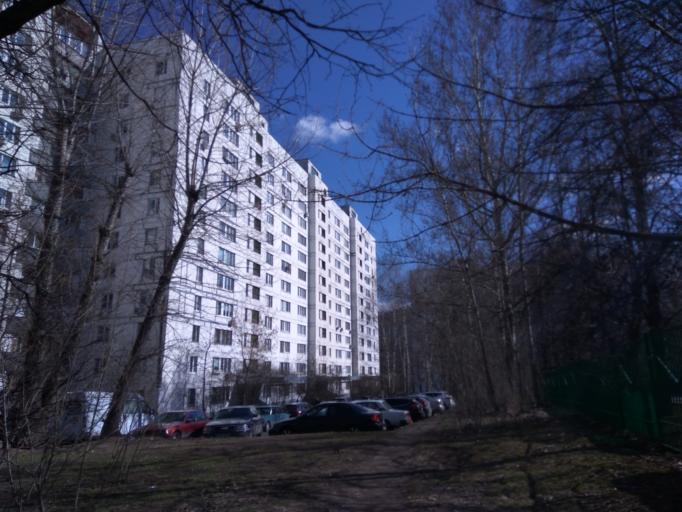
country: RU
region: Moscow
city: Ivanovskoye
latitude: 55.7811
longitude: 37.8341
